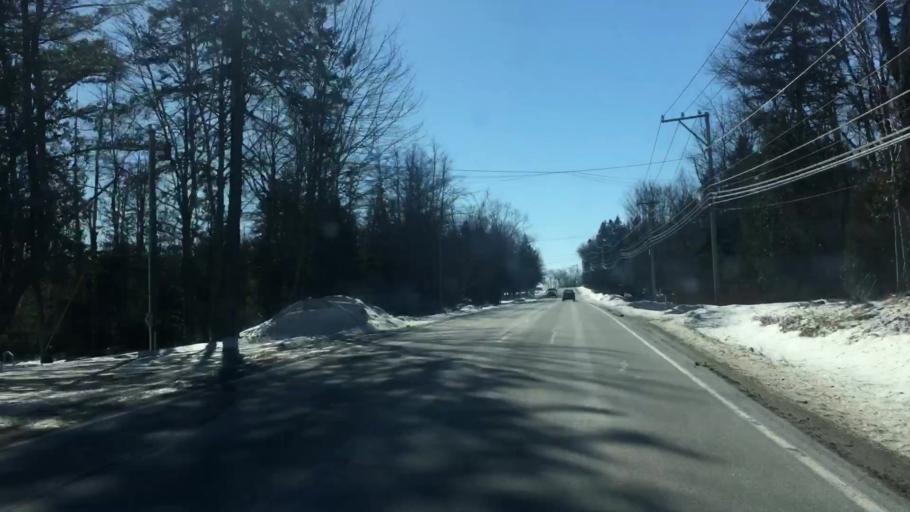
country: US
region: Maine
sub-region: Hancock County
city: Ellsworth
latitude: 44.5128
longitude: -68.4360
